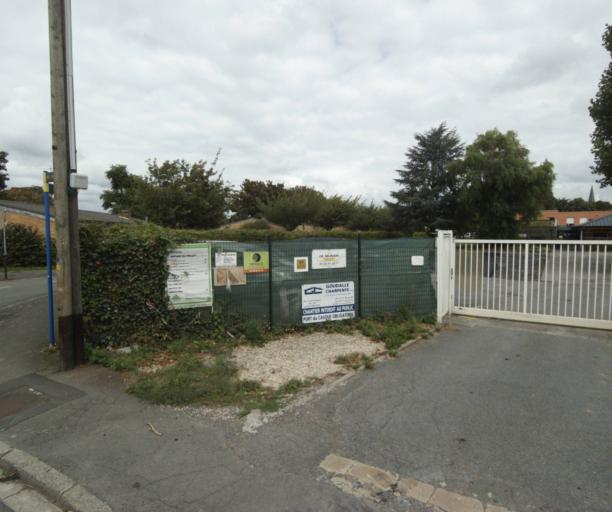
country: FR
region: Nord-Pas-de-Calais
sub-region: Departement du Nord
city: Villeneuve-d'Ascq
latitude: 50.6172
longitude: 3.1553
